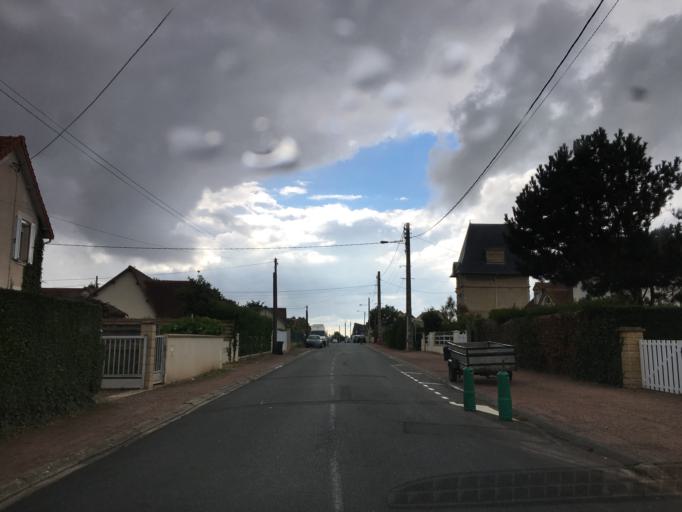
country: FR
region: Lower Normandy
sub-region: Departement du Calvados
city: Saint-Aubin-sur-Mer
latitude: 49.3328
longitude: -0.3987
